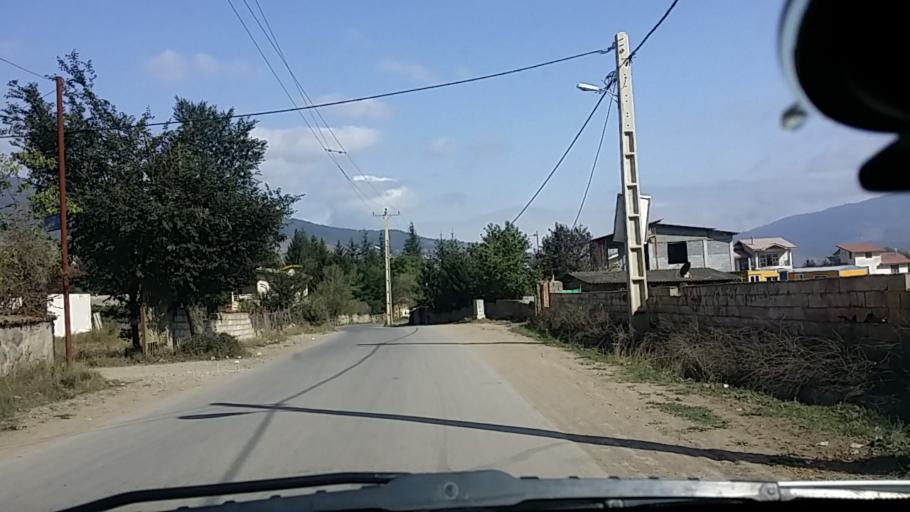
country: IR
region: Mazandaran
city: `Abbasabad
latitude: 36.5028
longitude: 51.1730
